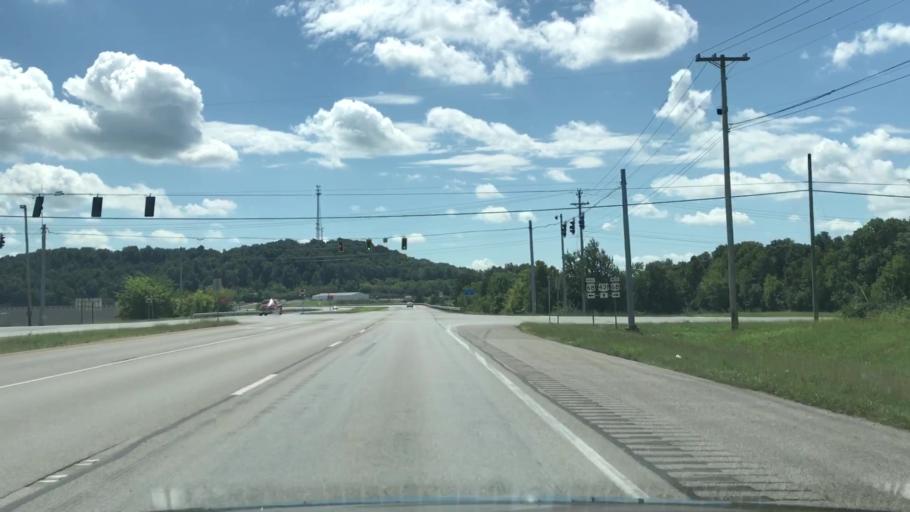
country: US
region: Kentucky
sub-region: Logan County
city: Russellville
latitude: 36.8401
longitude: -86.9190
